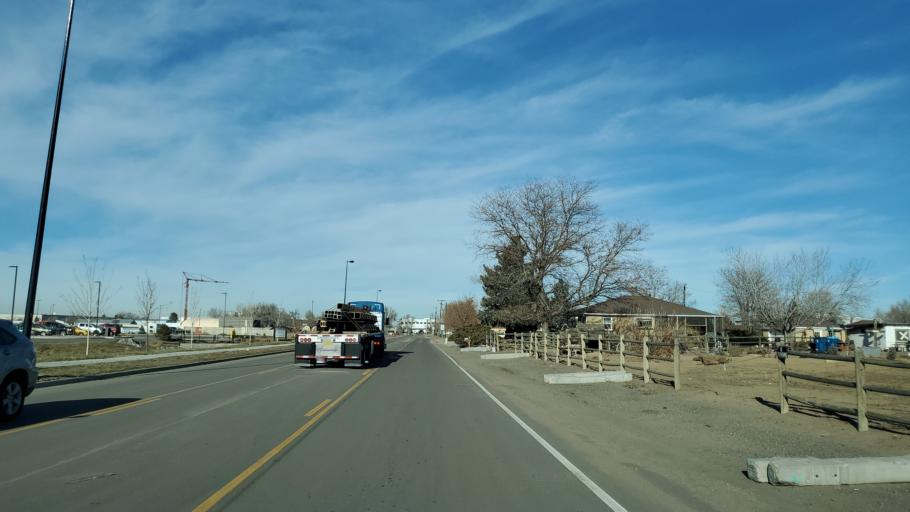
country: US
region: Colorado
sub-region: Adams County
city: Derby
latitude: 39.8510
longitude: -104.8938
